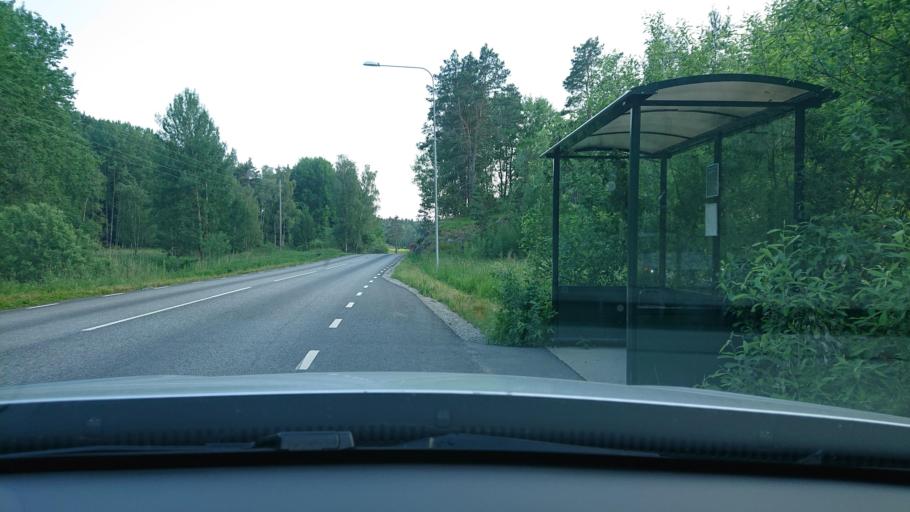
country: SE
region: Stockholm
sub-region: Vaxholms Kommun
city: Resaro
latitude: 59.4779
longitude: 18.3854
